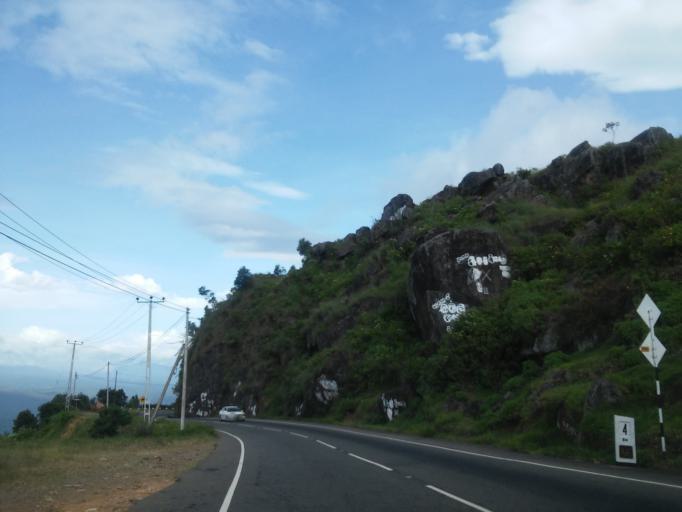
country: LK
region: Uva
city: Haputale
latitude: 6.7590
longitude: 80.9462
